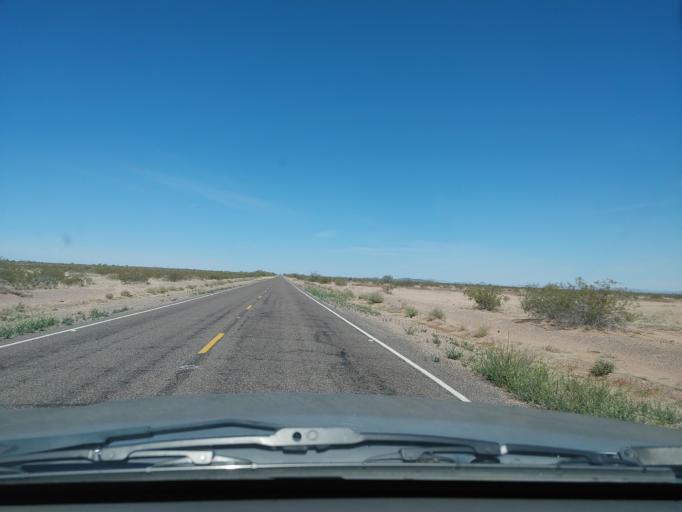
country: US
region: Arizona
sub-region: Maricopa County
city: Gila Bend
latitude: 32.8747
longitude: -113.2174
